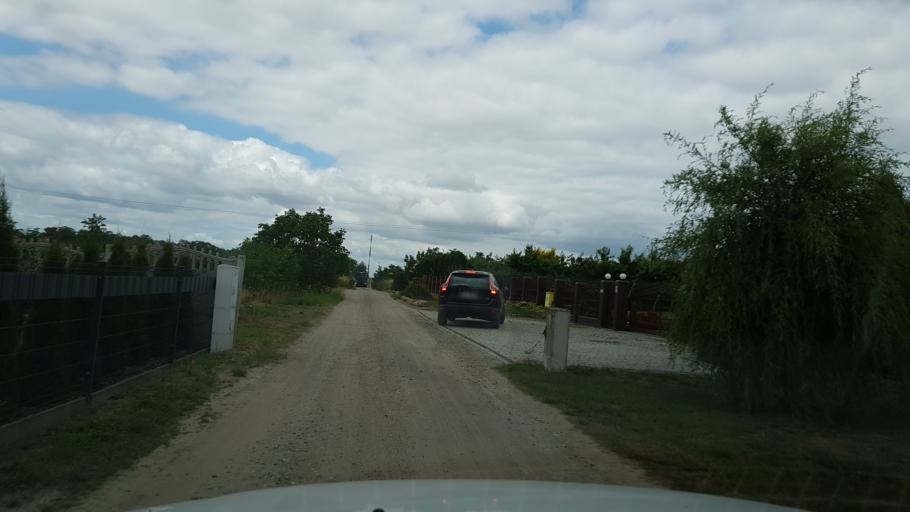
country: PL
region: West Pomeranian Voivodeship
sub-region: Powiat mysliborski
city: Mysliborz
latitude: 52.9302
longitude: 14.8797
